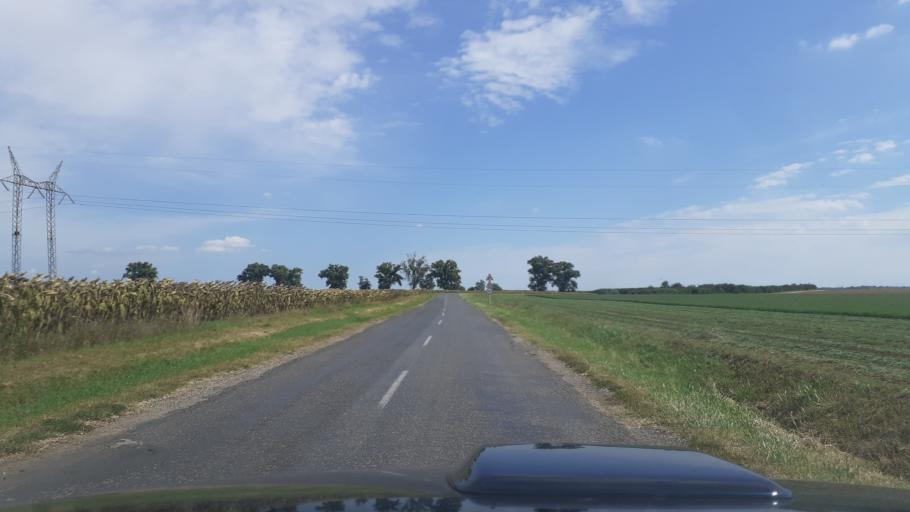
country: HU
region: Fejer
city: Seregelyes
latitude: 47.1509
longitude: 18.5799
